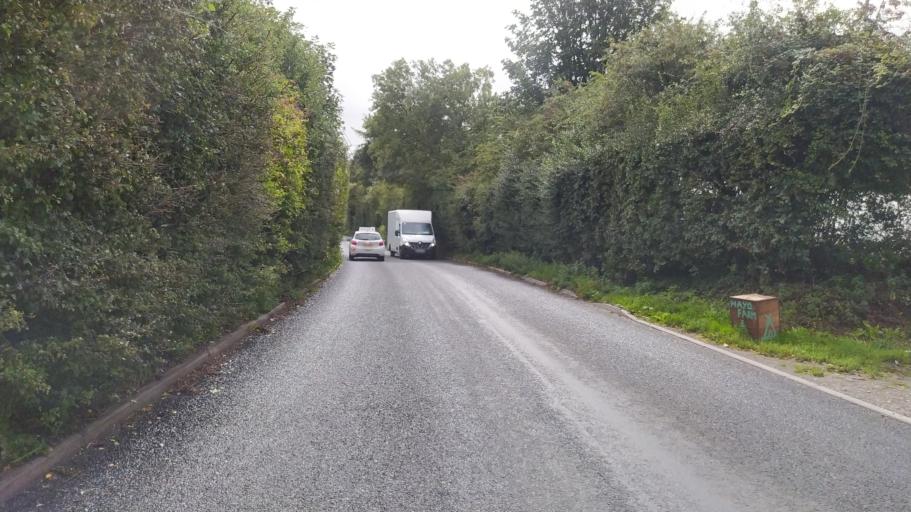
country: GB
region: England
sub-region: Dorset
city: Shaftesbury
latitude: 50.9988
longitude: -2.1791
